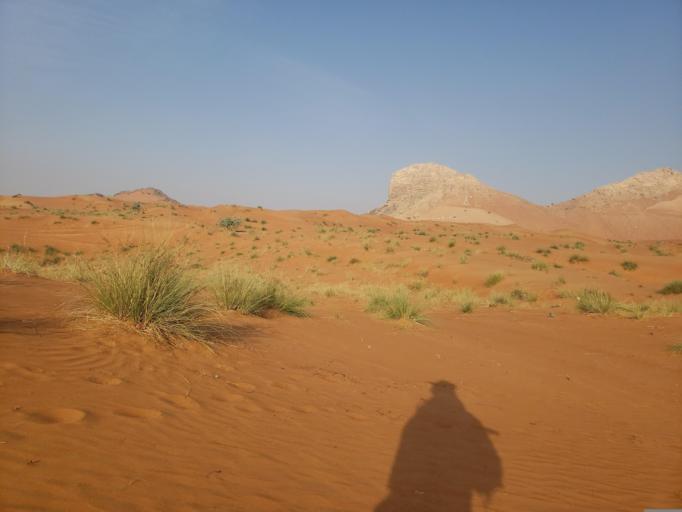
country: AE
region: Ash Shariqah
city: Adh Dhayd
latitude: 25.1374
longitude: 55.8424
